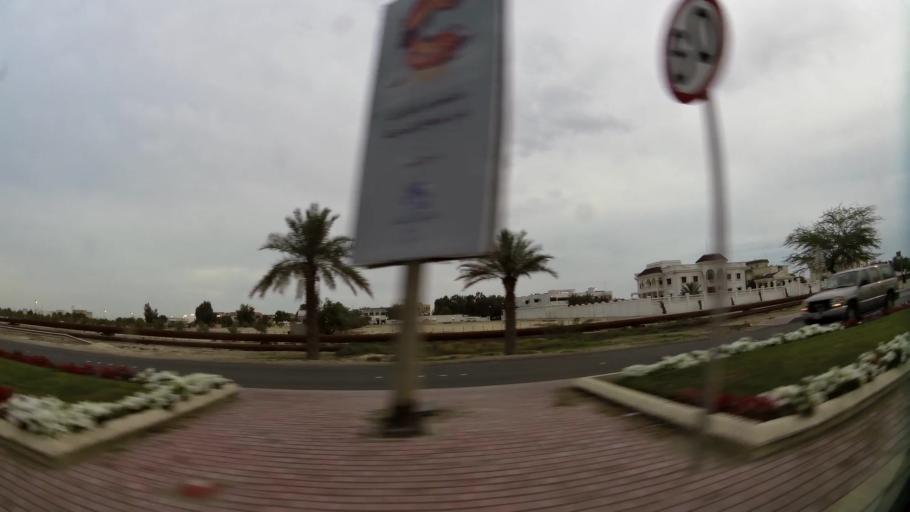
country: BH
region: Northern
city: Ar Rifa'
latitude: 26.1348
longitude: 50.5335
